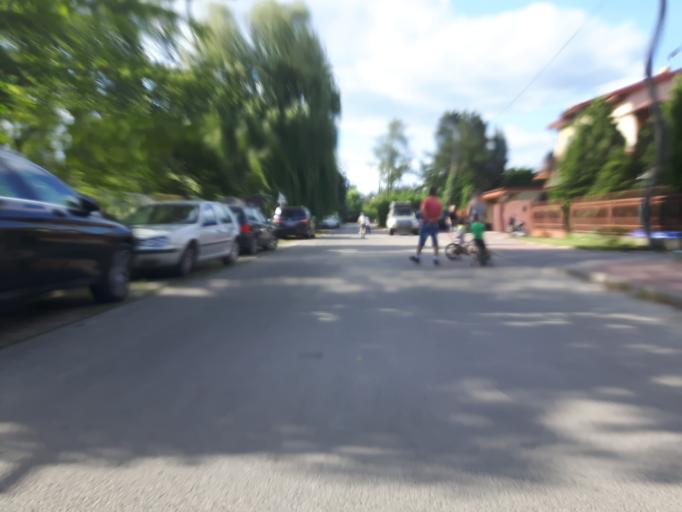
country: PL
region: Masovian Voivodeship
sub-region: Powiat wolominski
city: Zabki
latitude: 52.2928
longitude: 21.1235
